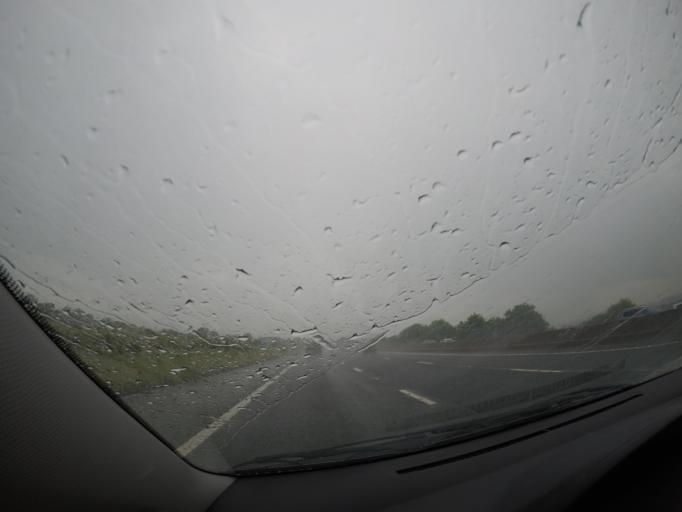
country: GB
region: England
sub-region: Cumbria
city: Penrith
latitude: 54.6847
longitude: -2.7895
